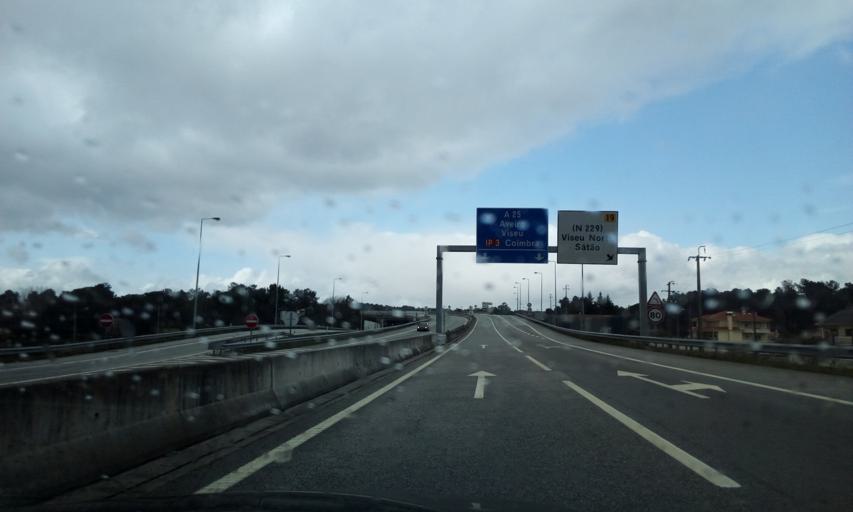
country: PT
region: Viseu
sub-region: Viseu
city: Rio de Loba
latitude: 40.6504
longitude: -7.8610
